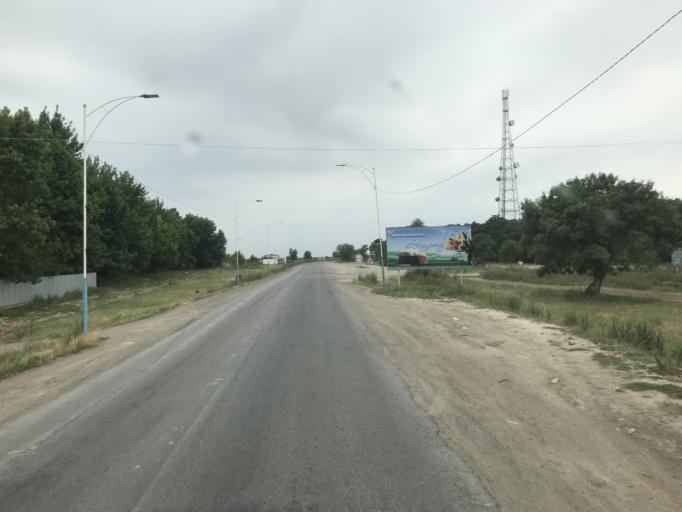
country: KZ
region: Ongtustik Qazaqstan
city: Ilyich
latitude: 40.9562
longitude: 68.4636
